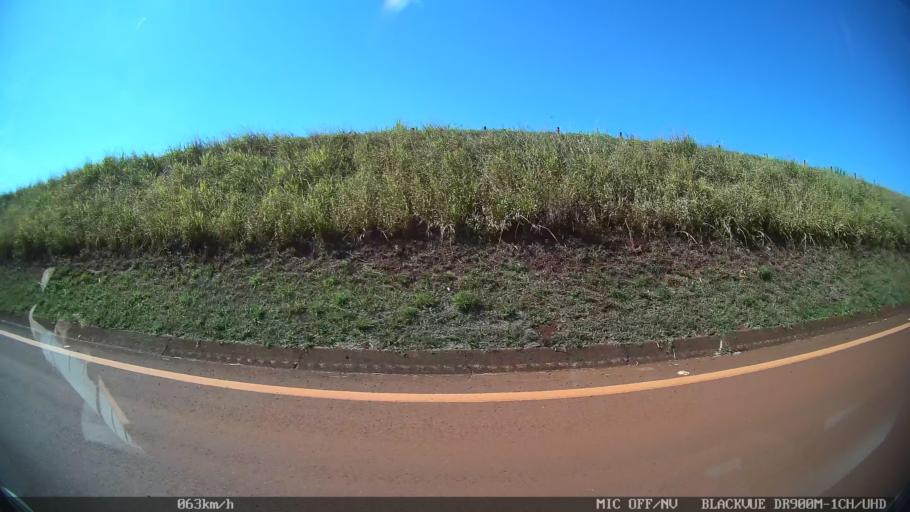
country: BR
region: Sao Paulo
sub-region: Franca
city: Franca
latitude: -20.6734
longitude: -47.4950
